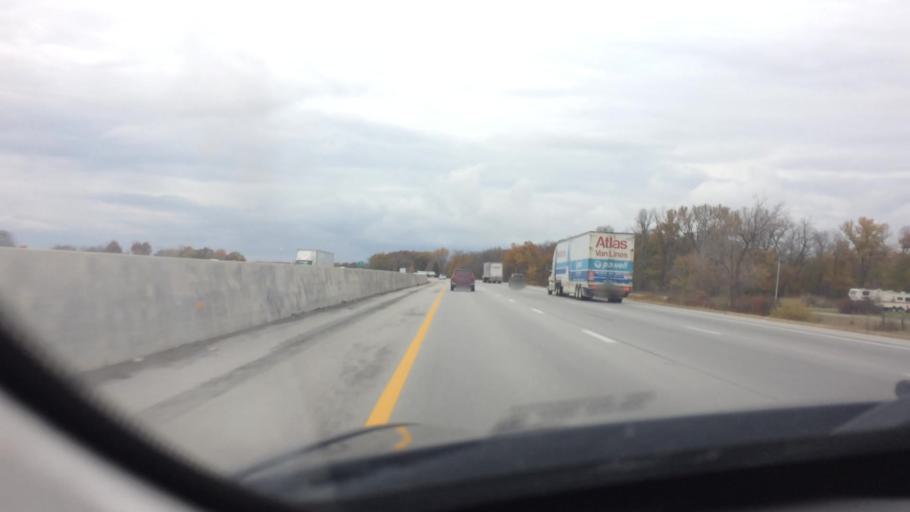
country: US
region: Ohio
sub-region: Wood County
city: North Baltimore
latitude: 41.2149
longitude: -83.6498
